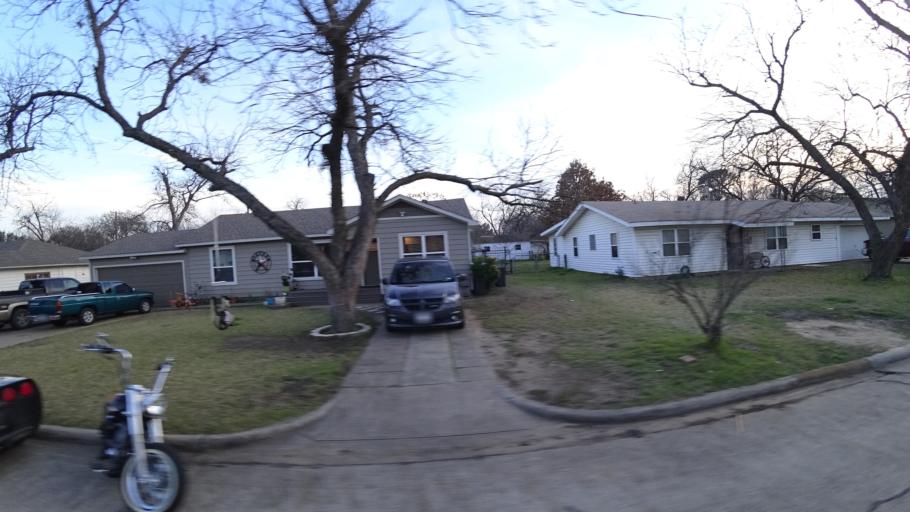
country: US
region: Texas
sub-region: Denton County
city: Lewisville
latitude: 33.0429
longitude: -97.0001
